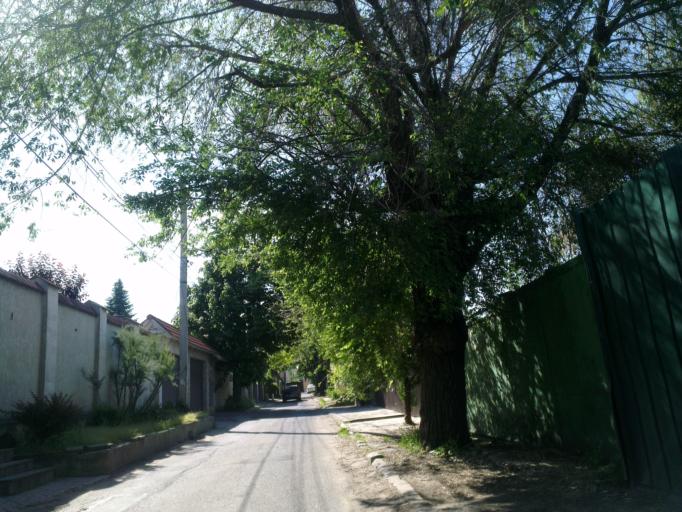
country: MD
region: Chisinau
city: Chisinau
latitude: 47.0150
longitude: 28.8244
